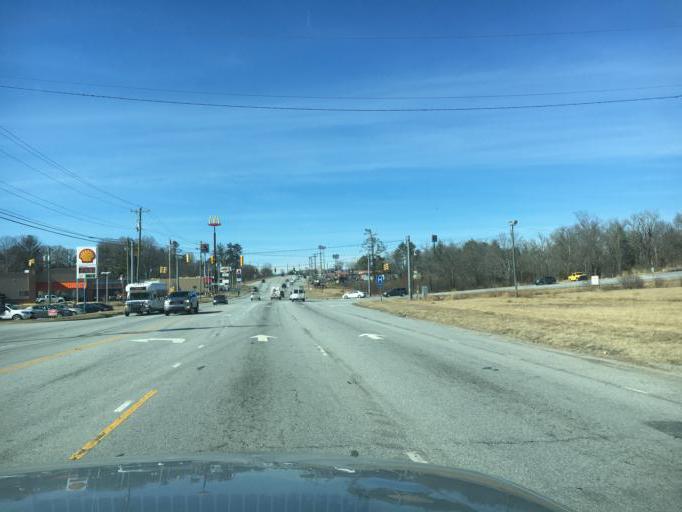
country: US
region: North Carolina
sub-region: Henderson County
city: Mountain Home
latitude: 35.3946
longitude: -82.5045
